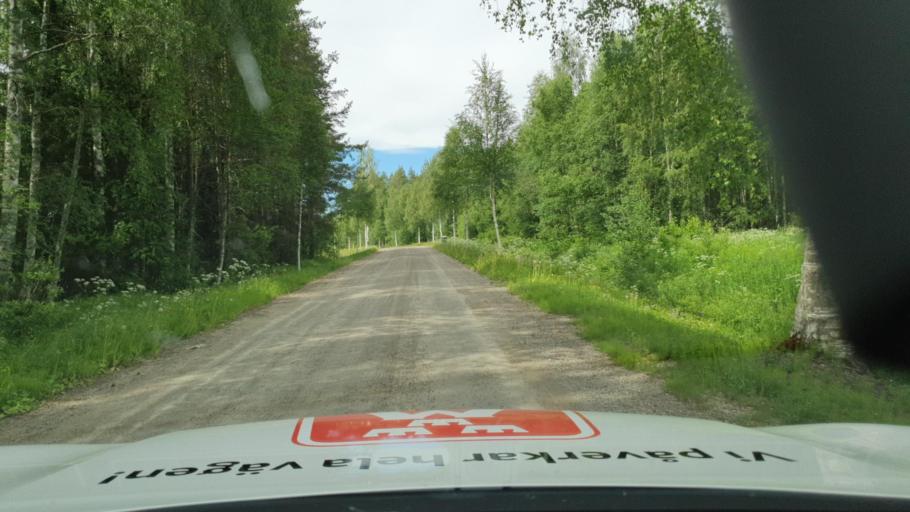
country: SE
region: Vaesterbotten
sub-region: Skelleftea Kommun
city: Burtraesk
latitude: 64.4780
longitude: 20.4391
